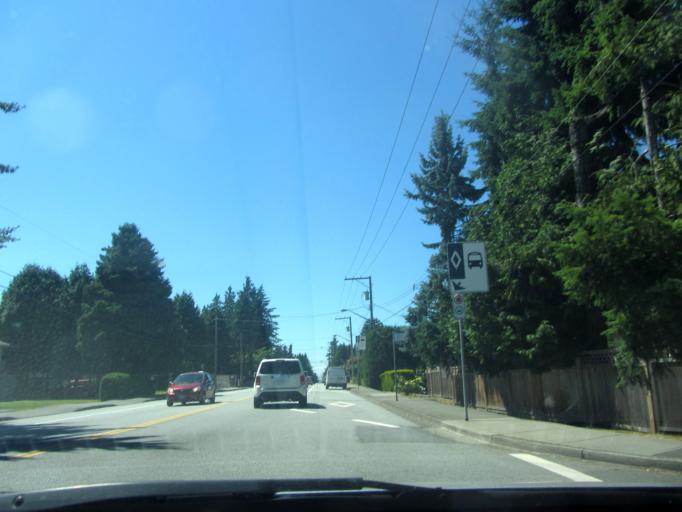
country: CA
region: British Columbia
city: Delta
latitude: 49.1342
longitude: -122.8961
